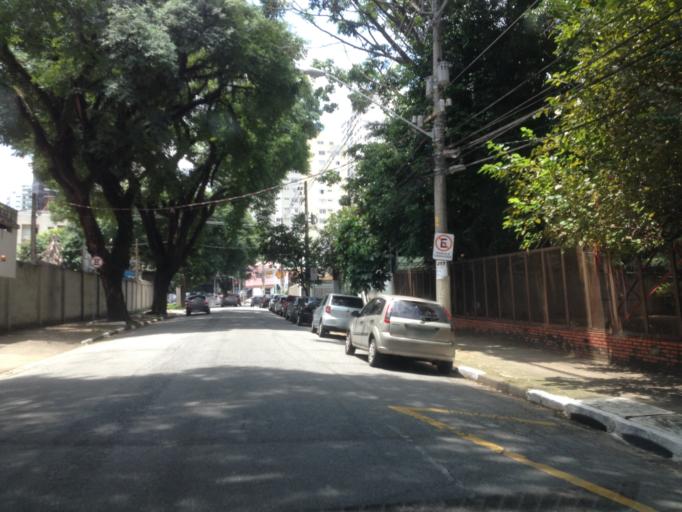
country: BR
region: Sao Paulo
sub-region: Sao Paulo
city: Sao Paulo
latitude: -23.5782
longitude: -46.6522
